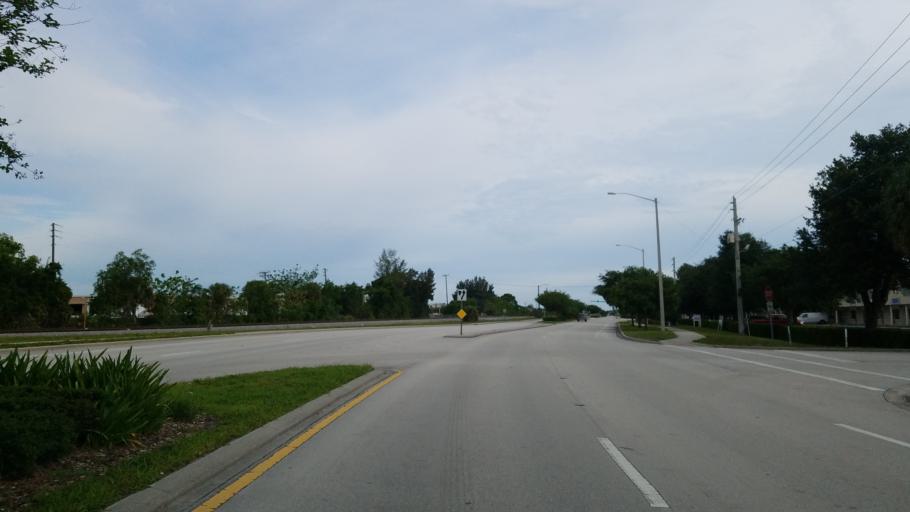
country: US
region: Florida
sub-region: Martin County
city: Stuart
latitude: 27.1741
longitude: -80.2289
